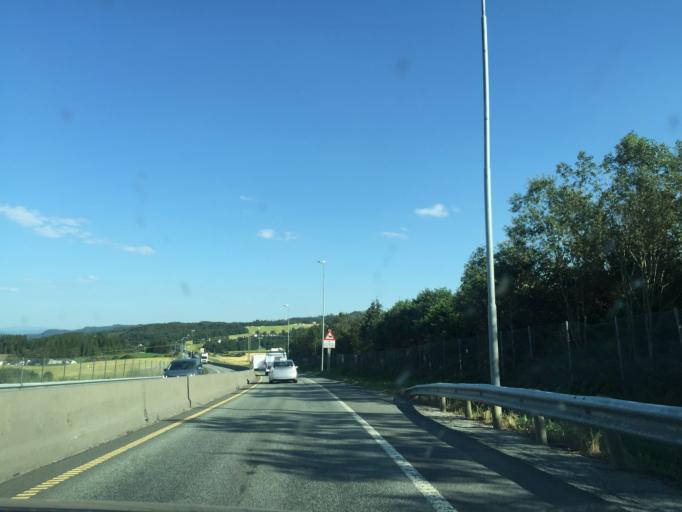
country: NO
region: Sor-Trondelag
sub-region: Malvik
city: Malvik
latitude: 63.4260
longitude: 10.6754
